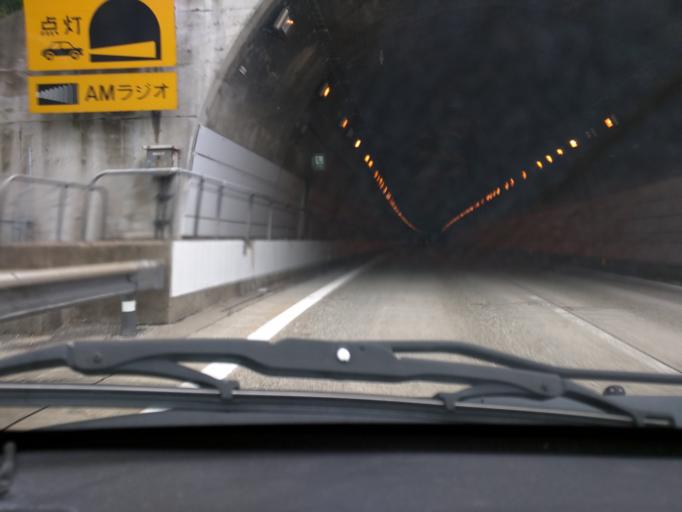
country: JP
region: Nagano
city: Nakano
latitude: 36.7987
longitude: 138.2826
